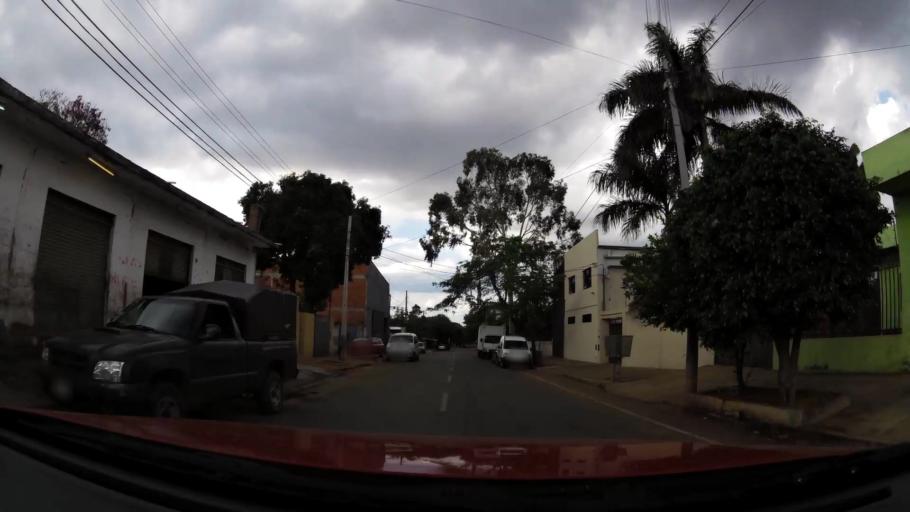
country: PY
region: Central
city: Fernando de la Mora
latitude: -25.3364
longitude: -57.5588
